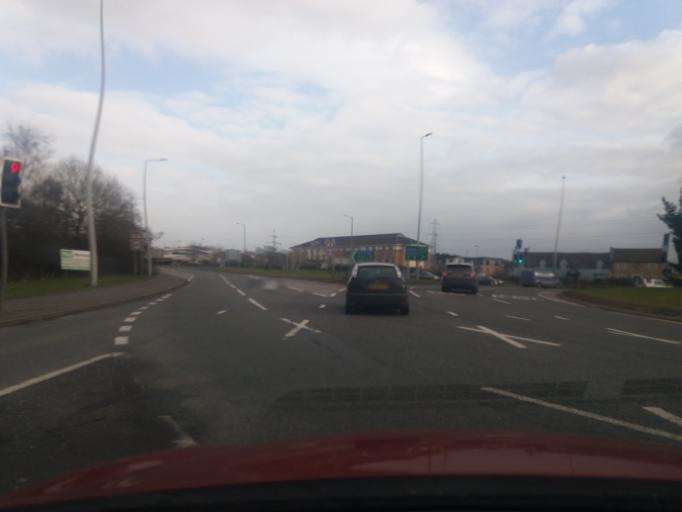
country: GB
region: England
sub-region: Lancashire
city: Clayton-le-Woods
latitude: 53.7220
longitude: -2.6730
